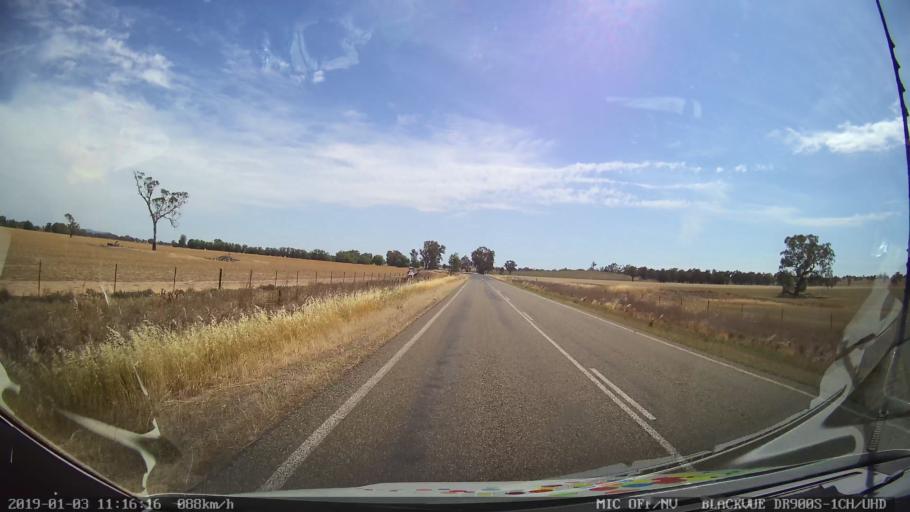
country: AU
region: New South Wales
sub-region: Young
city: Young
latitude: -34.1539
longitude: 148.2694
